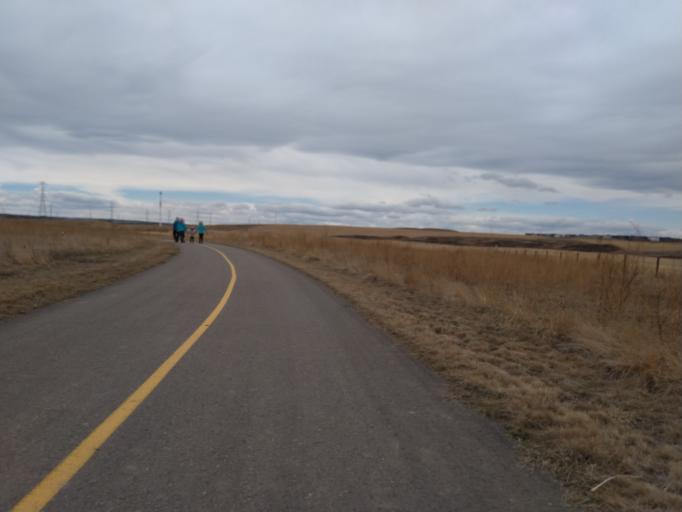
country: CA
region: Alberta
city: Airdrie
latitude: 51.1796
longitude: -114.0383
